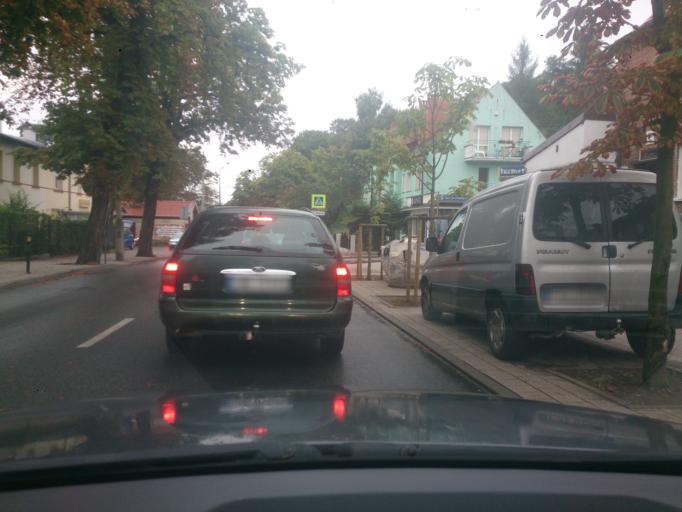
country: PL
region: Pomeranian Voivodeship
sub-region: Sopot
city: Sopot
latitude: 54.4503
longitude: 18.5531
